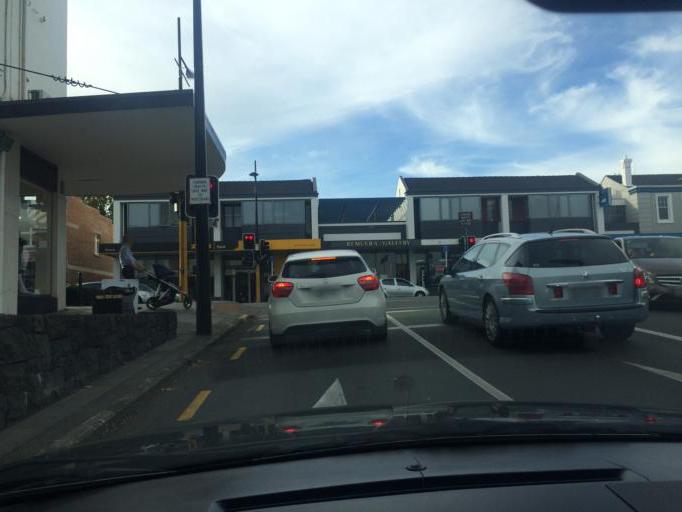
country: NZ
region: Auckland
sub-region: Auckland
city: Auckland
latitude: -36.8810
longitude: 174.7977
